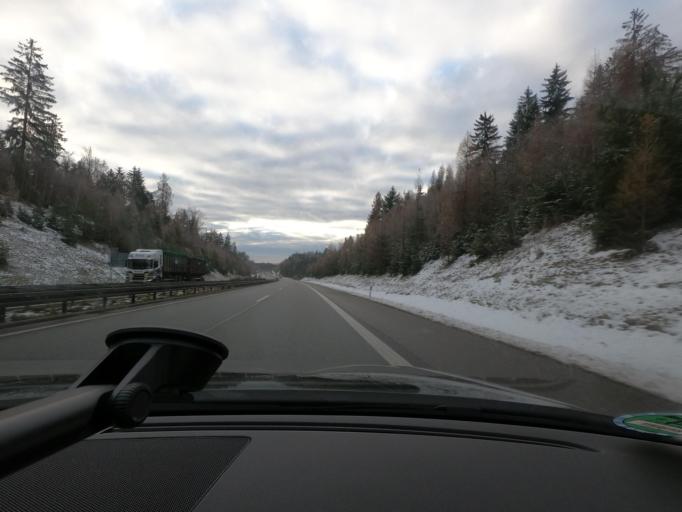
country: DE
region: Thuringia
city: Sankt Kilian
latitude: 50.5523
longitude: 10.7322
